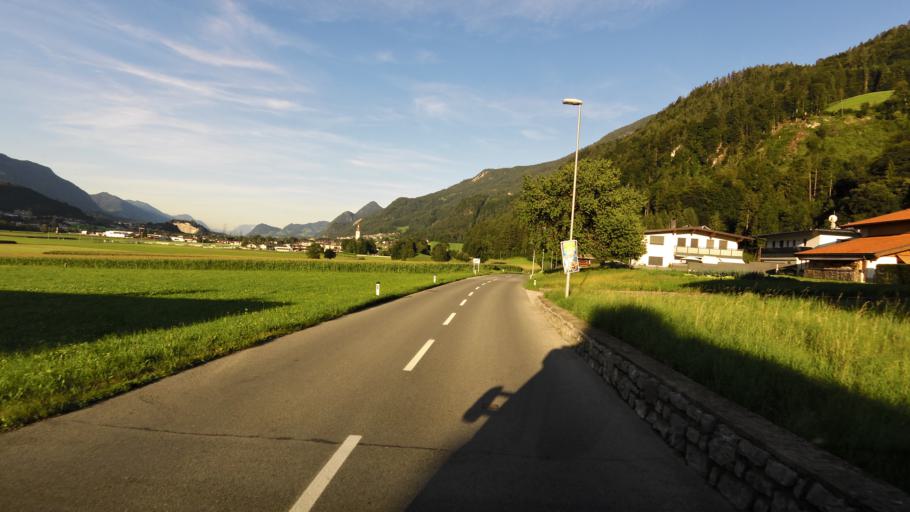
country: AT
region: Tyrol
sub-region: Politischer Bezirk Schwaz
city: Buch bei Jenbach
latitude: 47.3750
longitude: 11.7566
